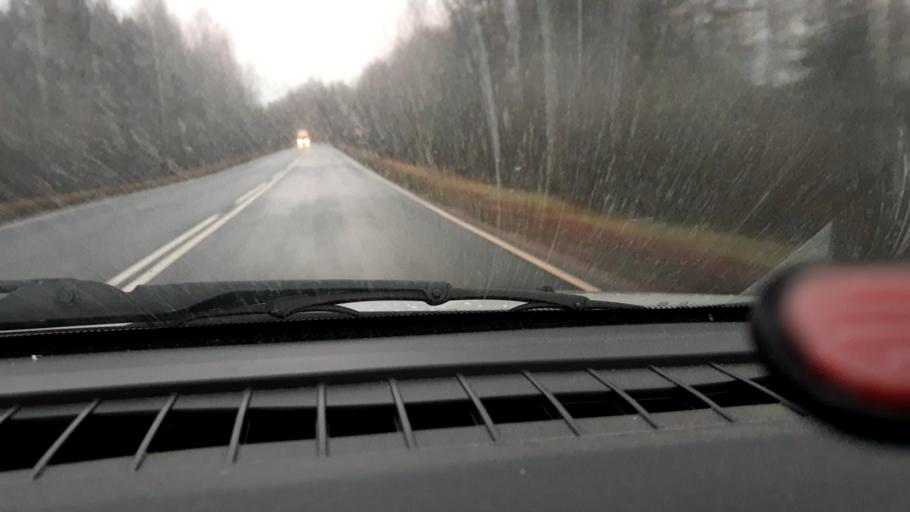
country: RU
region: Nizjnij Novgorod
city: Uren'
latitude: 57.2470
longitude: 45.5963
